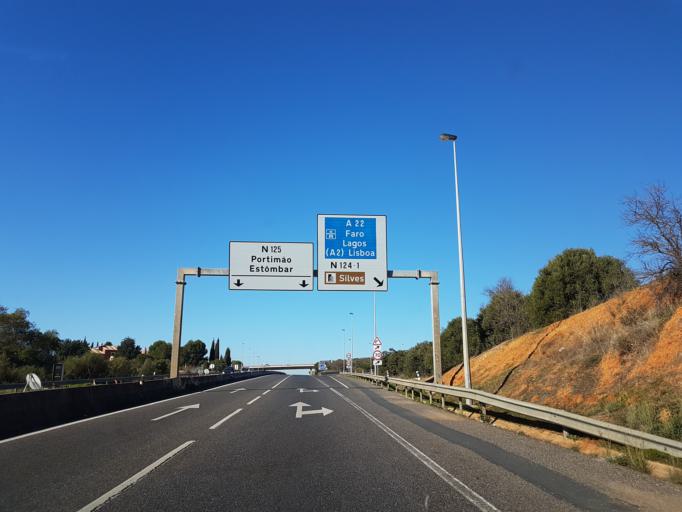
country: PT
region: Faro
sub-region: Lagoa
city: Lagoa
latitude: 37.1381
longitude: -8.4652
